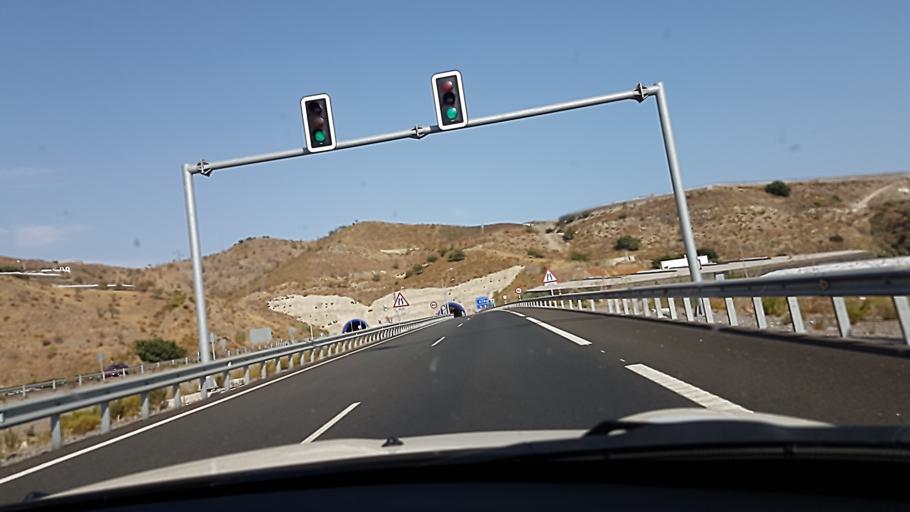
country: ES
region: Andalusia
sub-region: Provincia de Granada
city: Polopos
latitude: 36.7506
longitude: -3.3042
